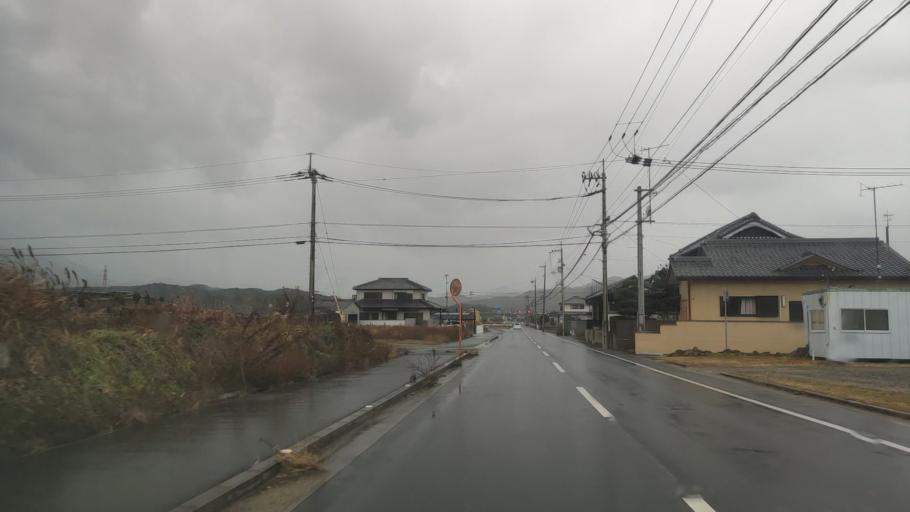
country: JP
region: Tokushima
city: Ishii
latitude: 34.2213
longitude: 134.3997
